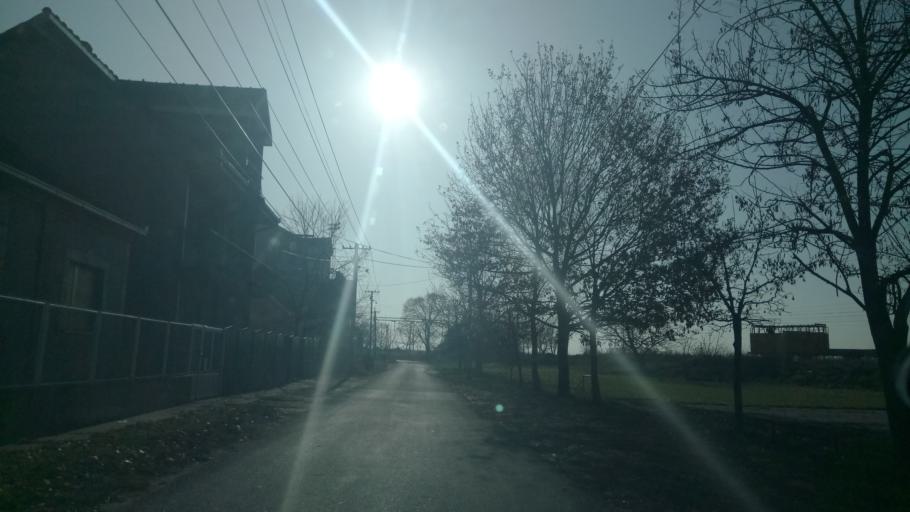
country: RS
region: Autonomna Pokrajina Vojvodina
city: Nova Pazova
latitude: 44.9401
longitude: 20.2077
